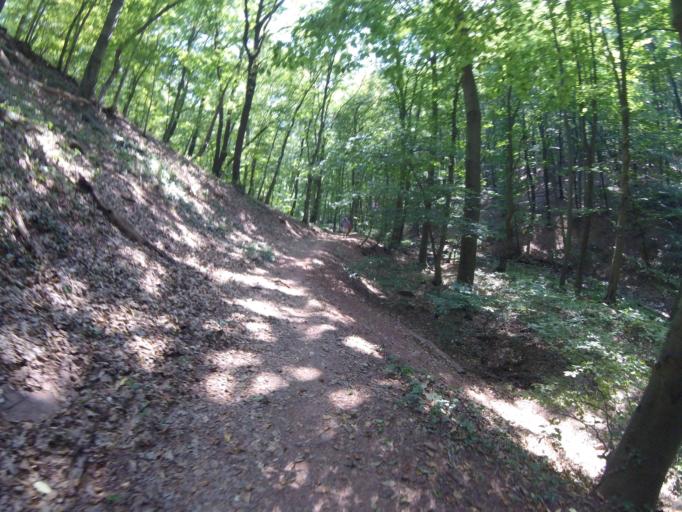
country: HU
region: Baranya
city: Pecs
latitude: 46.0950
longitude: 18.1723
